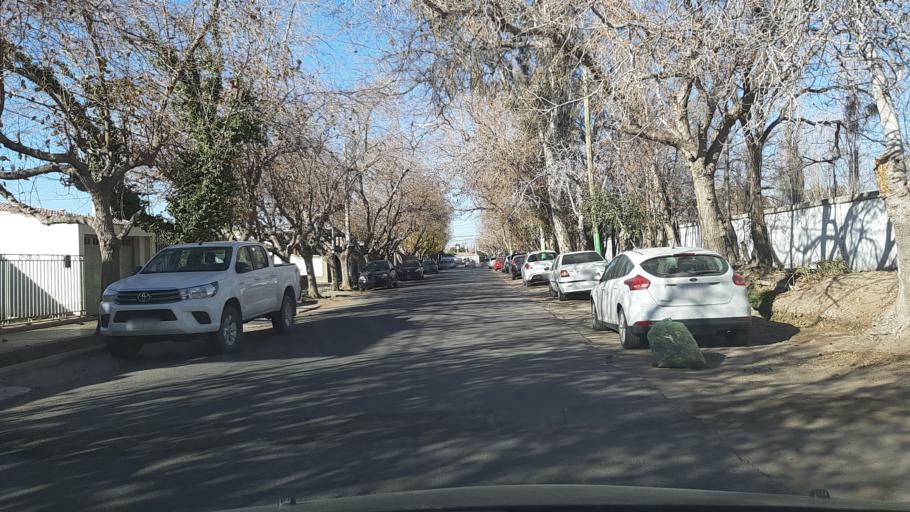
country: AR
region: San Juan
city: San Juan
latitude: -31.5286
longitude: -68.5916
